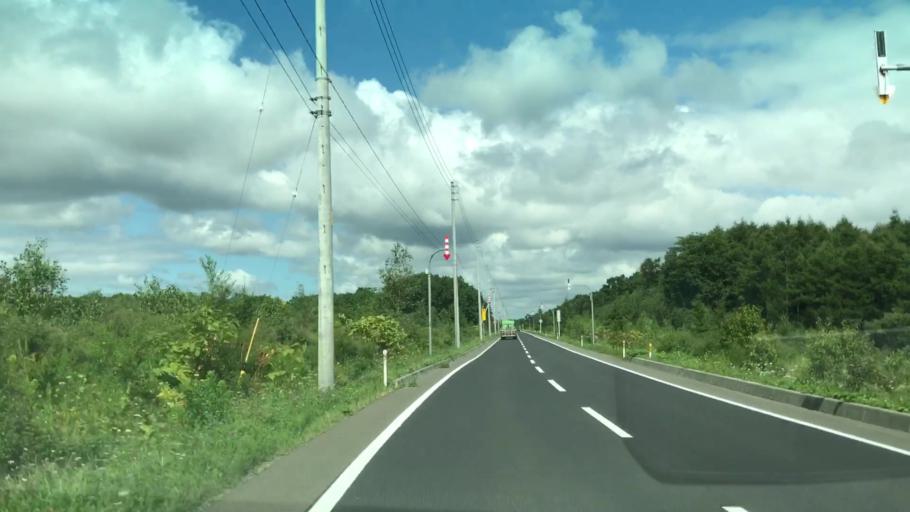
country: JP
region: Hokkaido
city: Chitose
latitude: 42.7645
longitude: 141.6643
